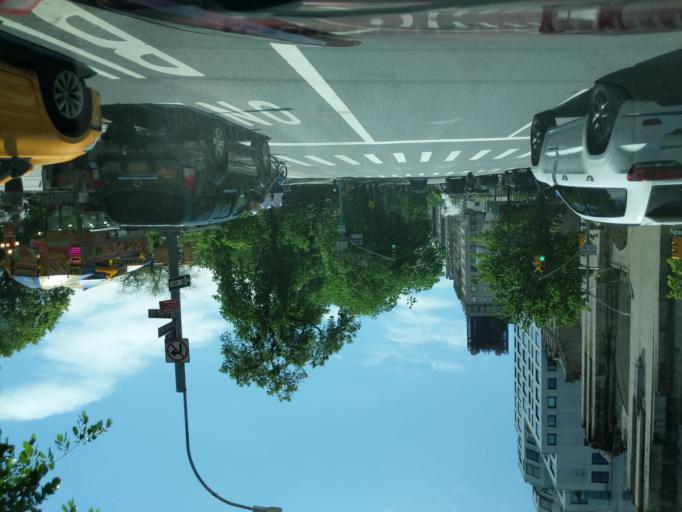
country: US
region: New York
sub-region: New York County
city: Manhattan
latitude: 40.7843
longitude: -73.9584
